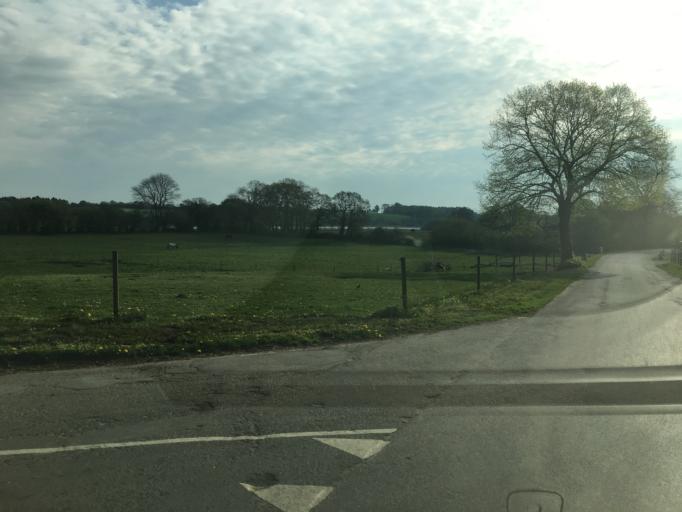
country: DK
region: South Denmark
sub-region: Haderslev Kommune
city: Vojens
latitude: 55.1875
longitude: 9.3873
